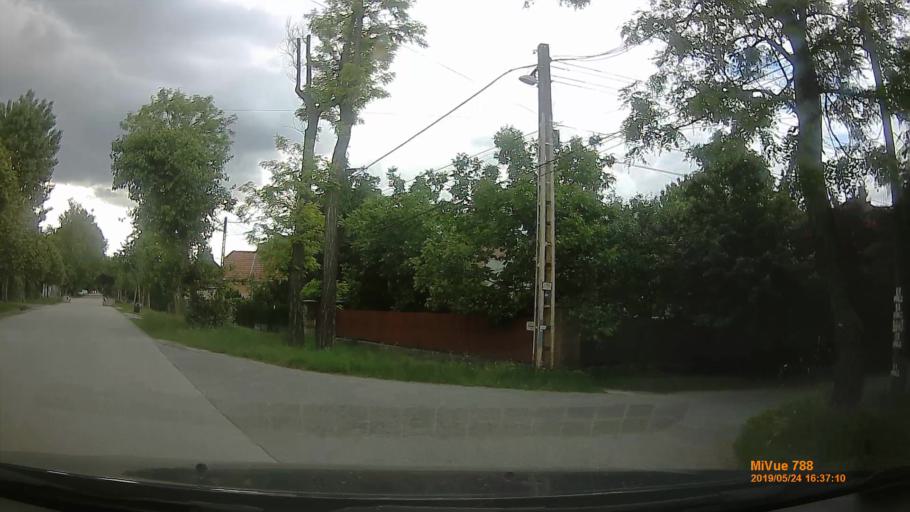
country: HU
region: Budapest
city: Budapest XVI. keruelet
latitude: 47.5089
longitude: 19.1640
